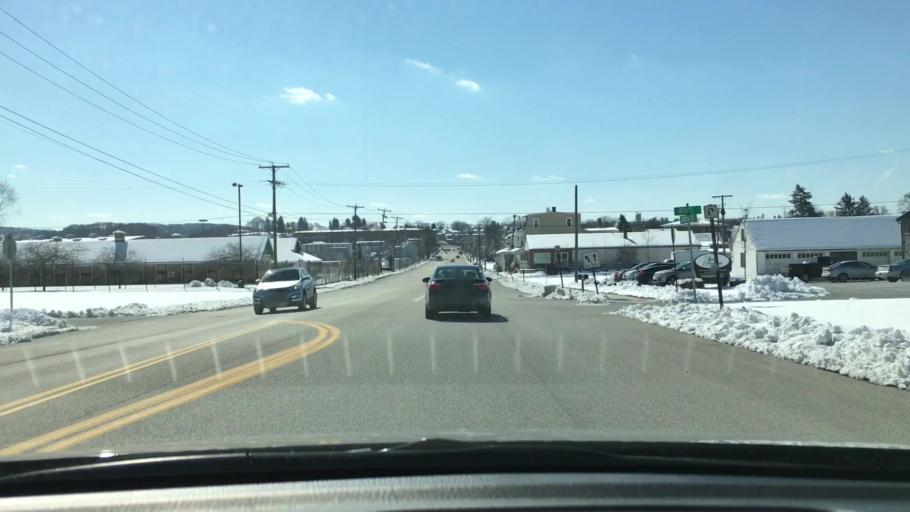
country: US
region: Pennsylvania
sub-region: York County
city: West York
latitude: 39.9604
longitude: -76.7599
